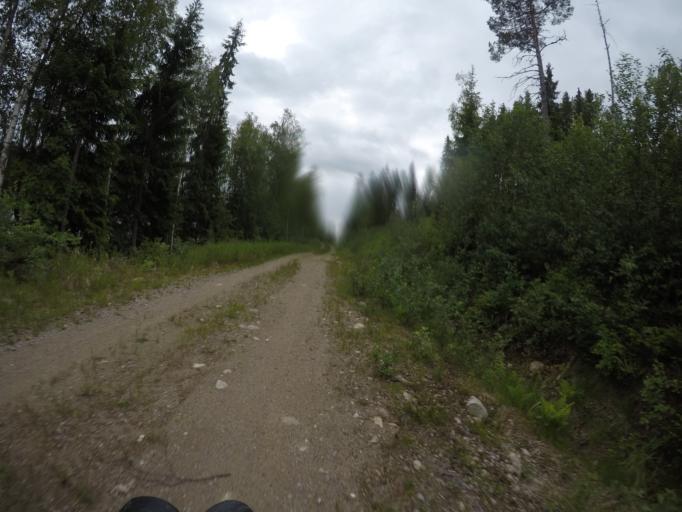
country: SE
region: Dalarna
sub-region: Ludvika Kommun
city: Abborrberget
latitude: 60.0491
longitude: 14.5897
